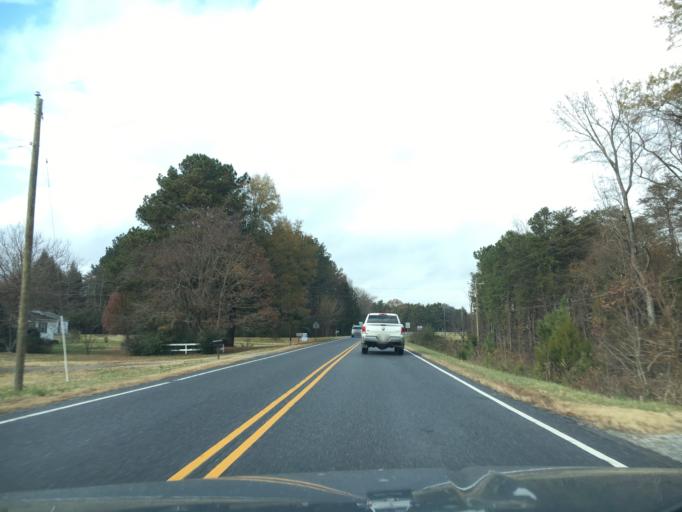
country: US
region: Virginia
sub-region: Prince Edward County
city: Farmville
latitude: 37.3352
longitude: -78.3880
